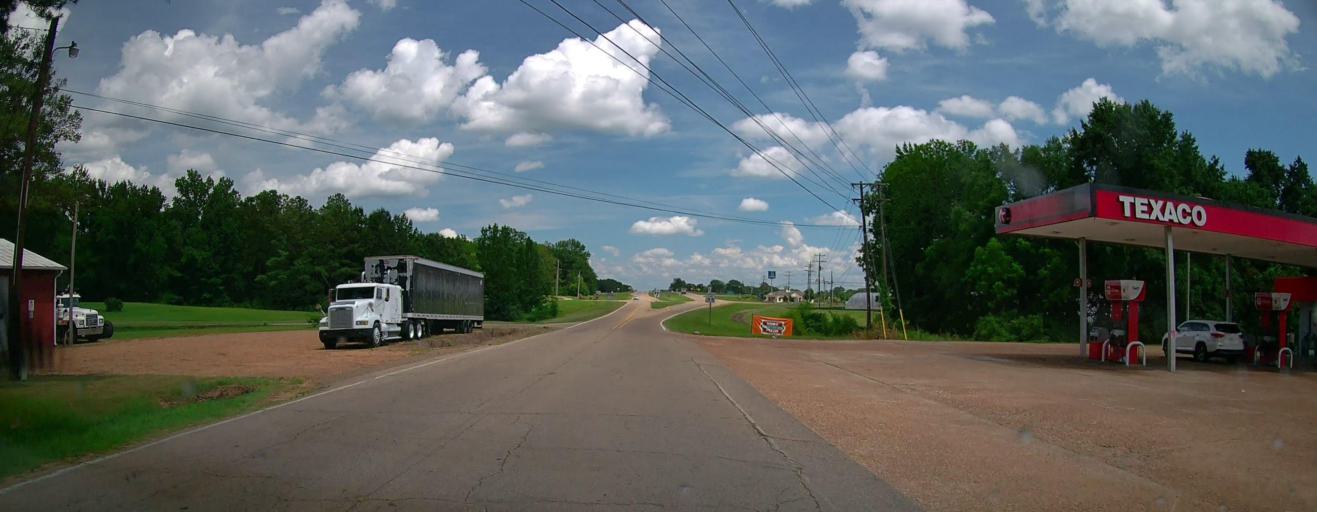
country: US
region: Mississippi
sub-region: Lee County
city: Shannon
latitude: 34.1196
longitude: -88.7082
